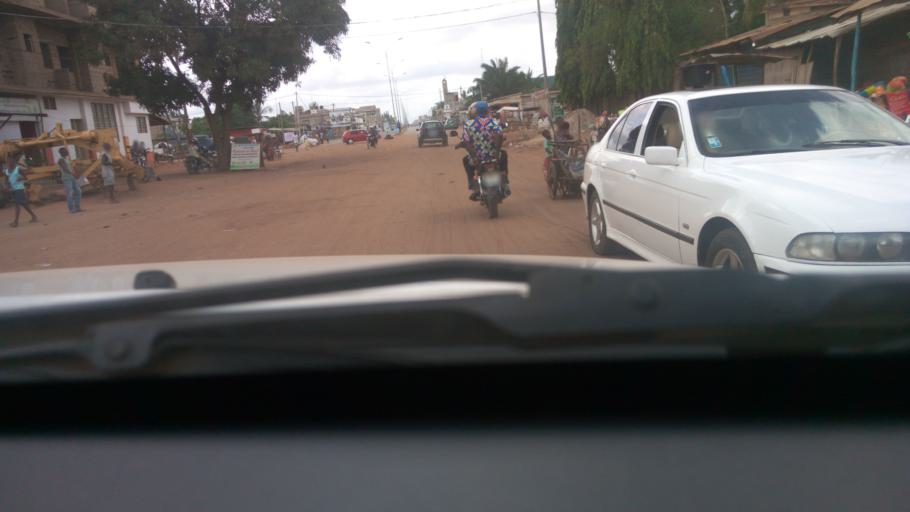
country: TG
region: Maritime
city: Lome
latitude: 6.2193
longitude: 1.1681
